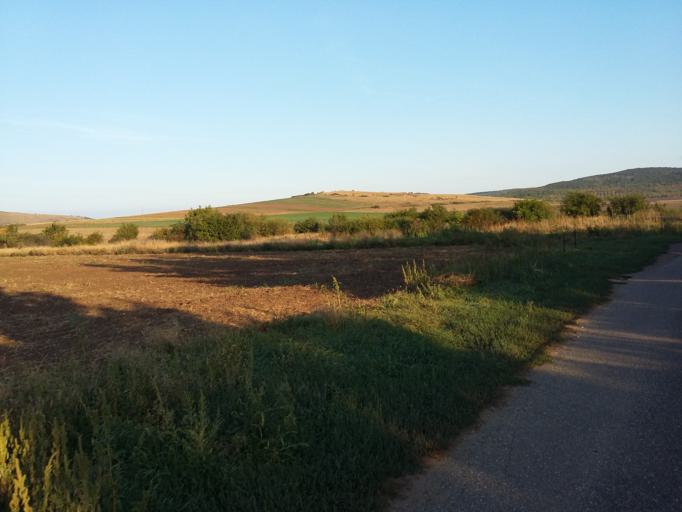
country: HU
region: Borsod-Abauj-Zemplen
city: Bekecs
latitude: 48.1632
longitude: 21.1809
